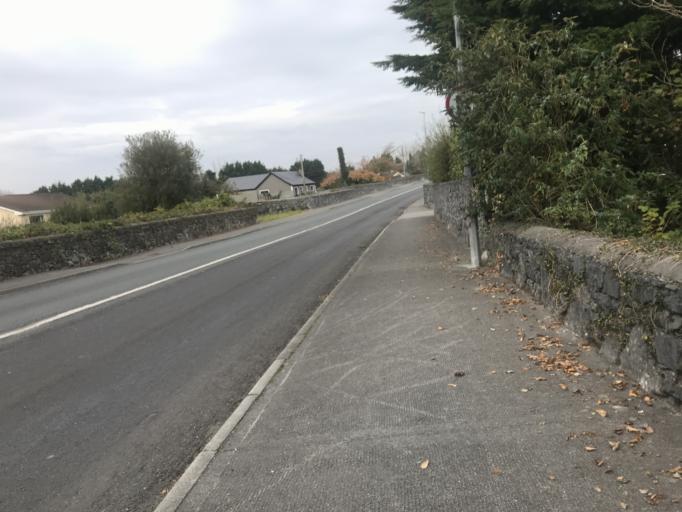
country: IE
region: Connaught
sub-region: County Galway
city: Gaillimh
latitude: 53.2952
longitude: -9.0535
